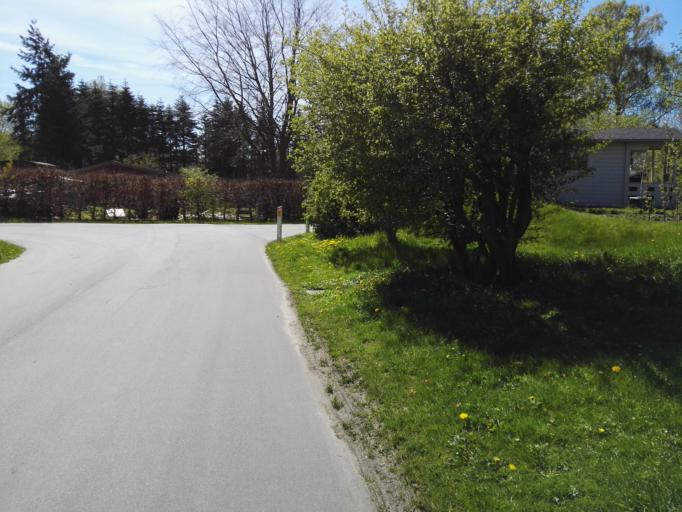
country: DK
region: Capital Region
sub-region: Frederikssund Kommune
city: Frederikssund
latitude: 55.8983
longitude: 12.0535
